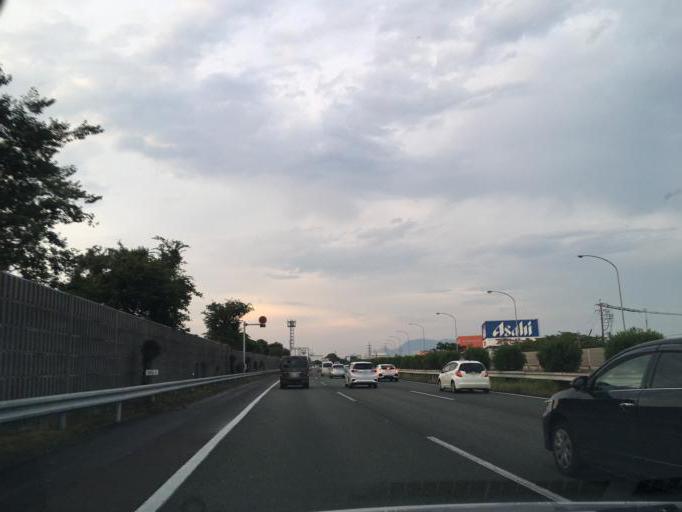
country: JP
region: Saga Prefecture
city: Tosu
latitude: 33.4055
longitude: 130.5378
